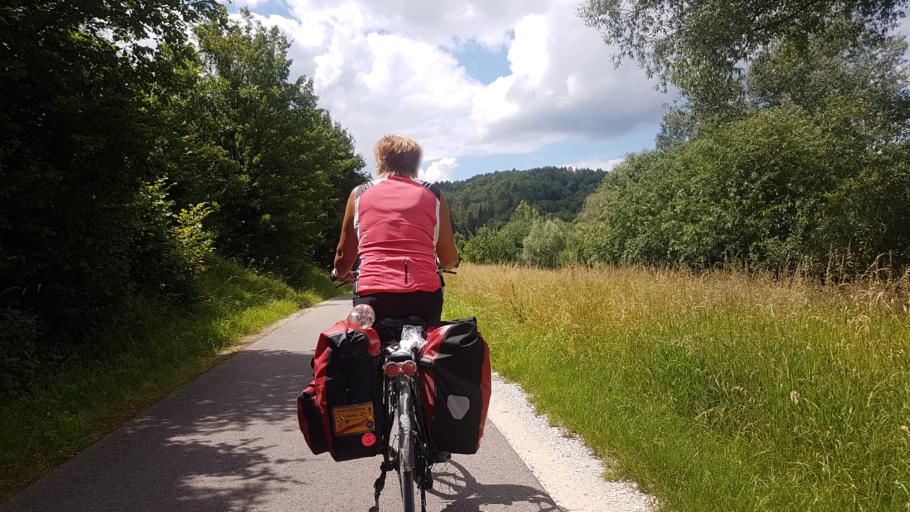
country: DE
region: Bavaria
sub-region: Regierungsbezirk Mittelfranken
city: Solnhofen
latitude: 48.8861
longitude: 11.0223
